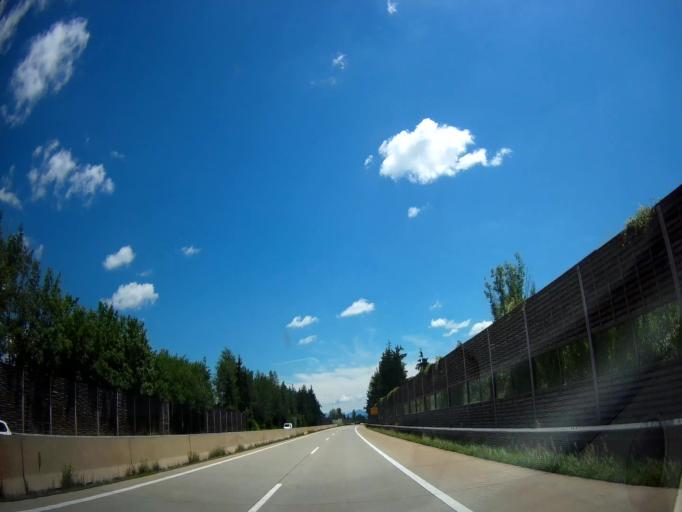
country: AT
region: Carinthia
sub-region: Politischer Bezirk Villach Land
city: Wernberg
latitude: 46.6227
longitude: 13.9733
